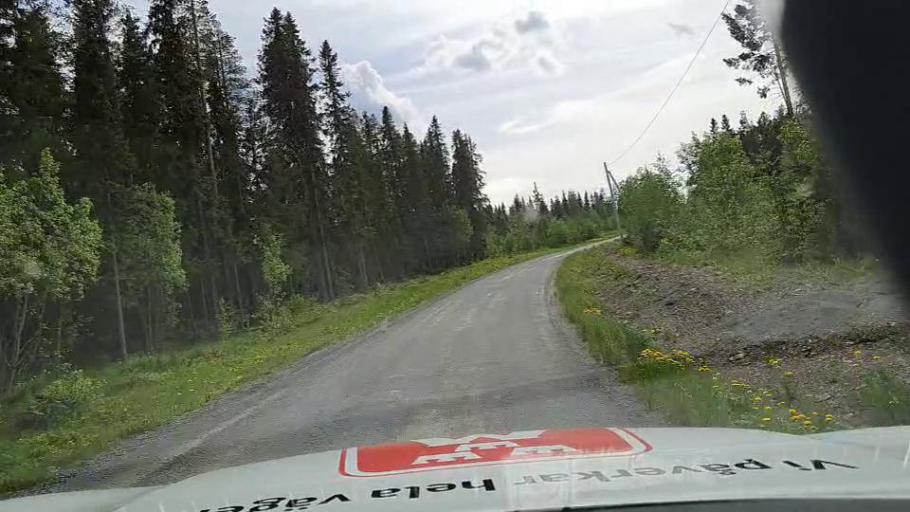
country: SE
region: Jaemtland
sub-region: OEstersunds Kommun
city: Brunflo
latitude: 62.9901
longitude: 14.7179
